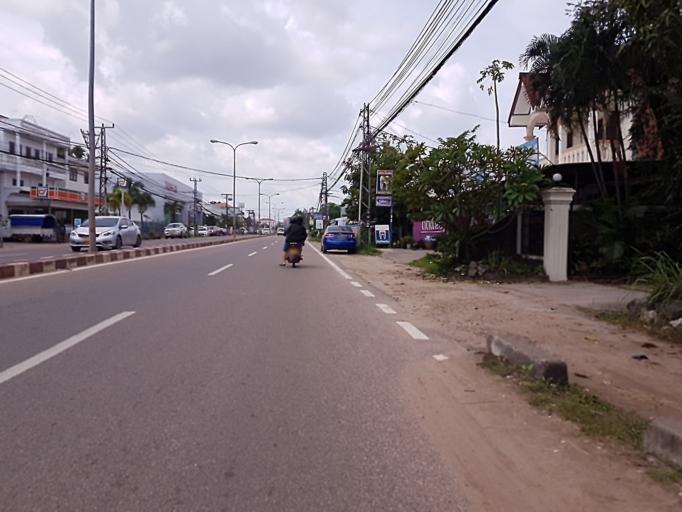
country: TH
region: Nong Khai
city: Si Chiang Mai
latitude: 17.9154
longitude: 102.6199
